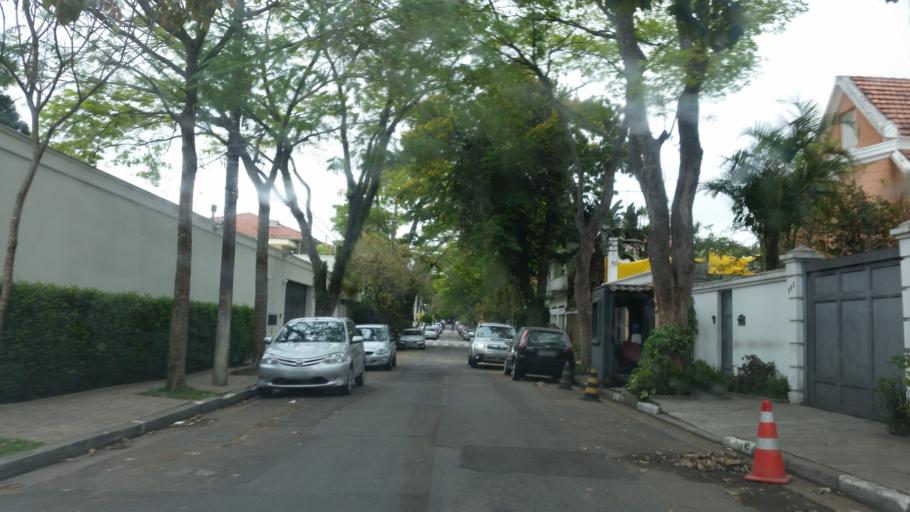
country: BR
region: Sao Paulo
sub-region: Sao Paulo
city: Sao Paulo
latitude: -23.5950
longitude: -46.6586
